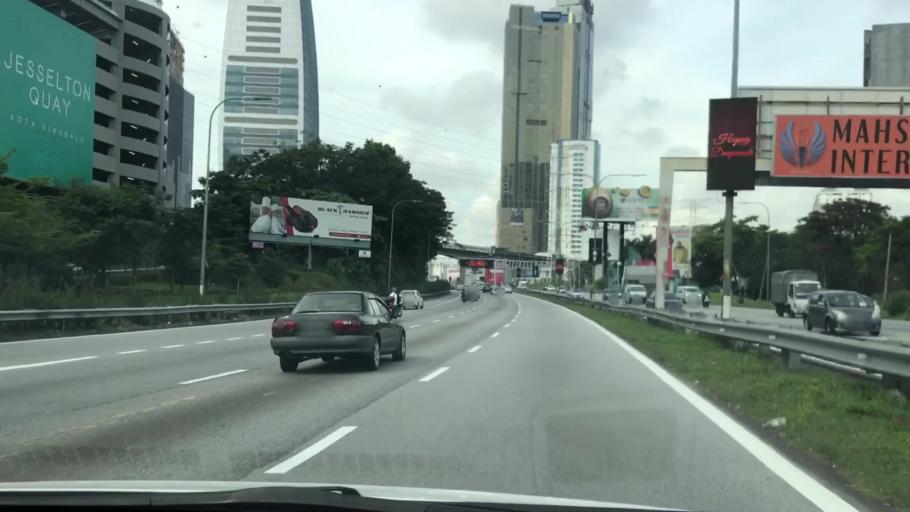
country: MY
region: Selangor
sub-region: Petaling
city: Petaling Jaya
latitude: 3.1059
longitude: 101.6454
